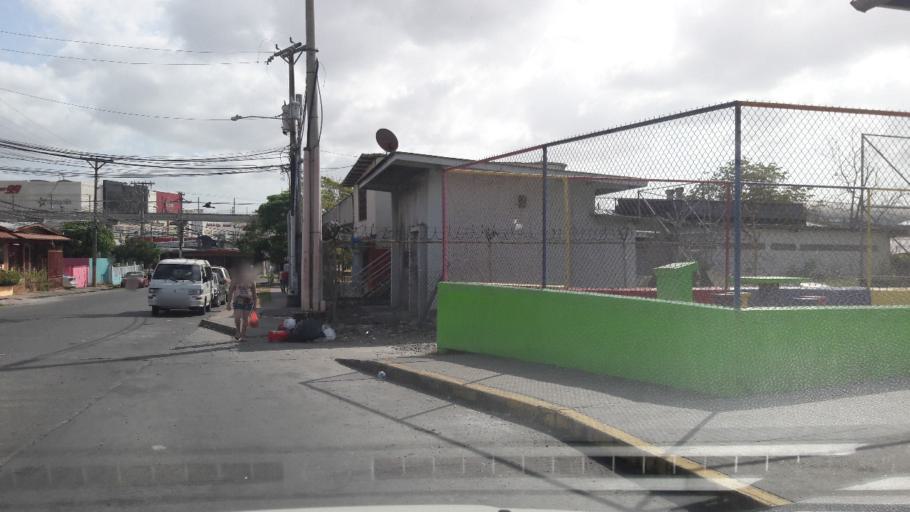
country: PA
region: Panama
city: San Miguelito
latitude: 9.0503
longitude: -79.5115
